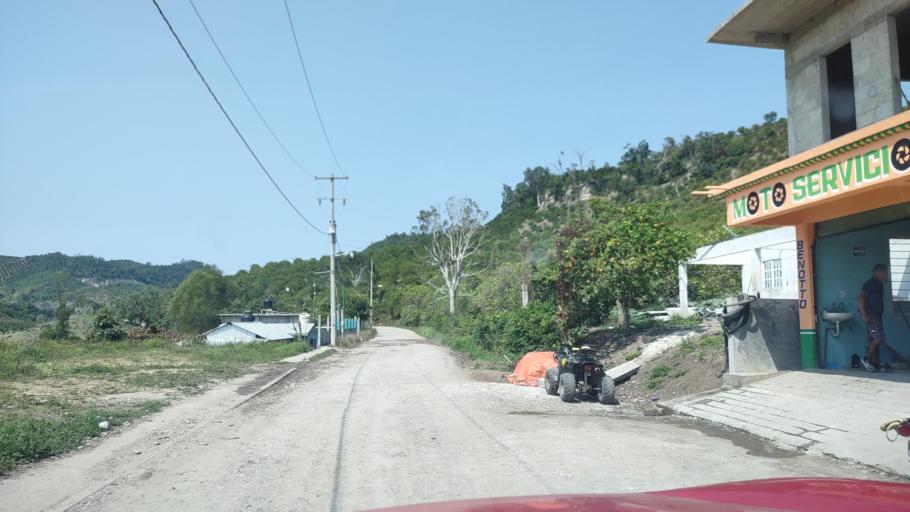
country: MX
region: Veracruz
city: Agua Dulce
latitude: 20.3172
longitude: -97.1755
